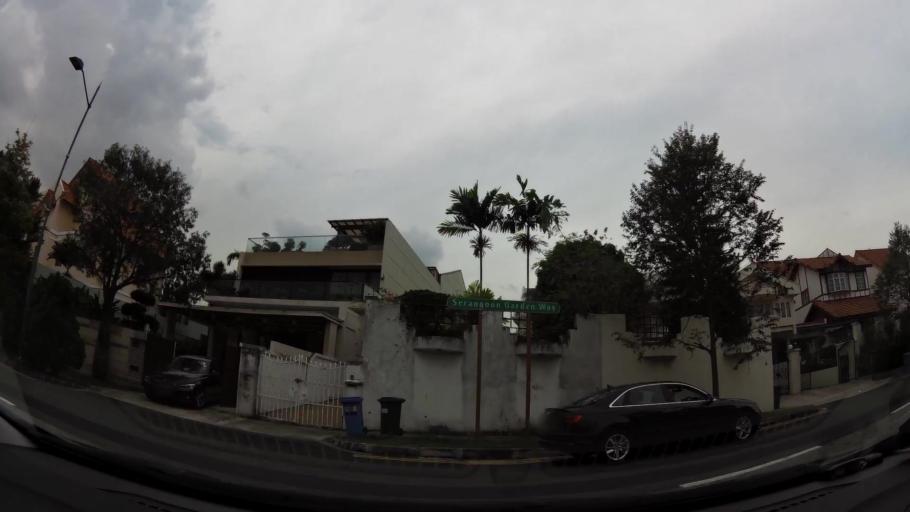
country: SG
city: Singapore
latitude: 1.3648
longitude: 103.8636
